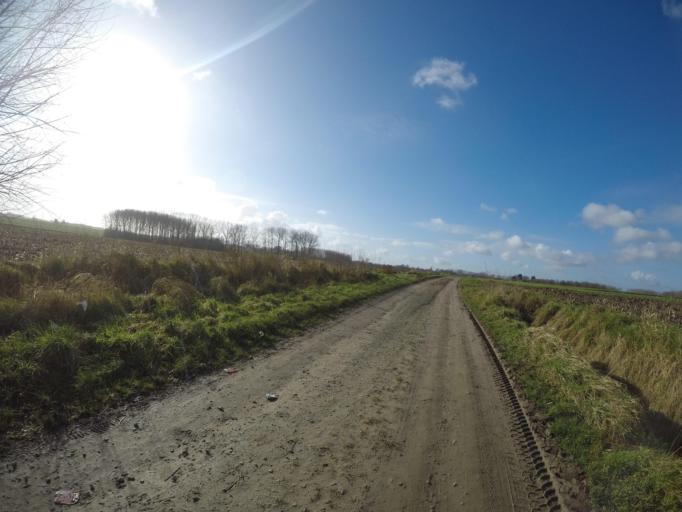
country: BE
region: Flanders
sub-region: Provincie Vlaams-Brabant
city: Sint-Martens-Lennik
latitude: 50.7867
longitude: 4.1908
